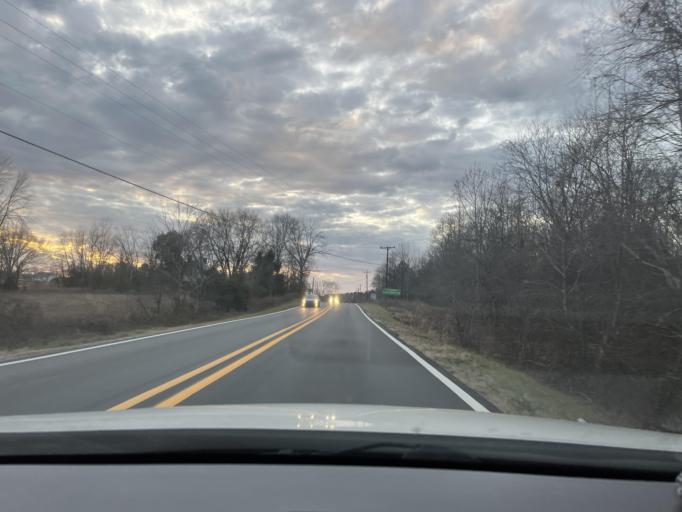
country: US
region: North Carolina
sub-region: Guilford County
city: Gibsonville
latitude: 36.0792
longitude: -79.5478
